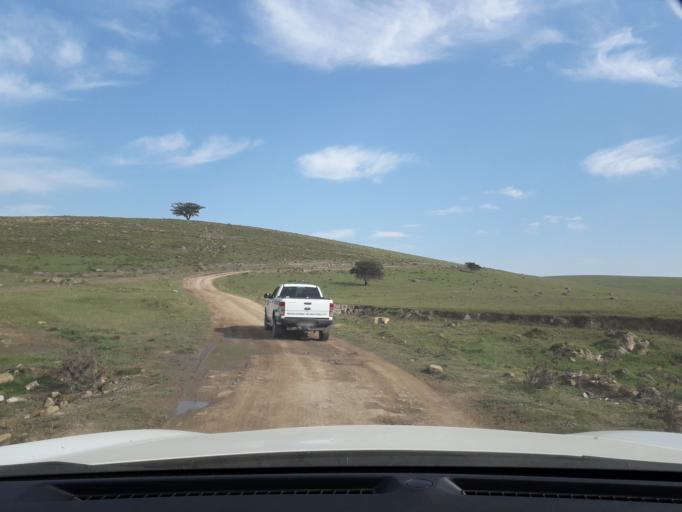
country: ZA
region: Eastern Cape
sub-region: Buffalo City Metropolitan Municipality
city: Bhisho
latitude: -33.0033
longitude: 27.3245
